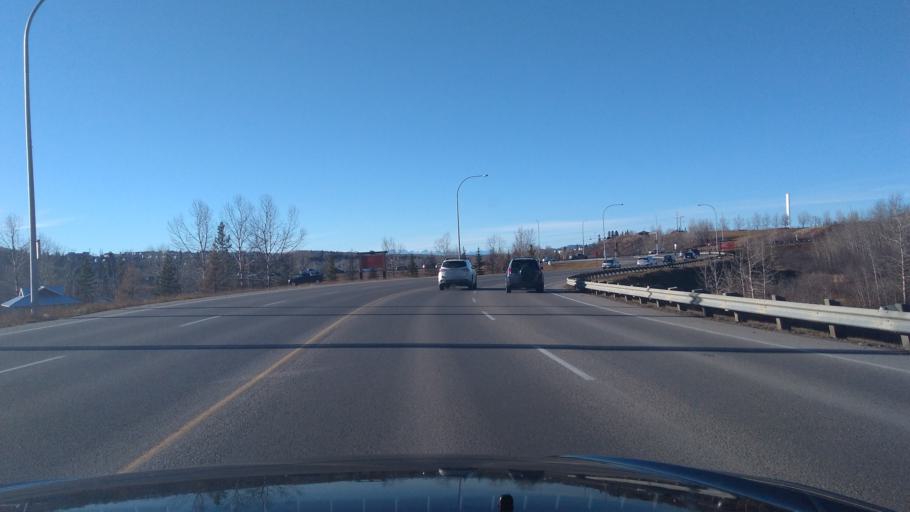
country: CA
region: Alberta
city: Cochrane
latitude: 51.1836
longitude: -114.4834
